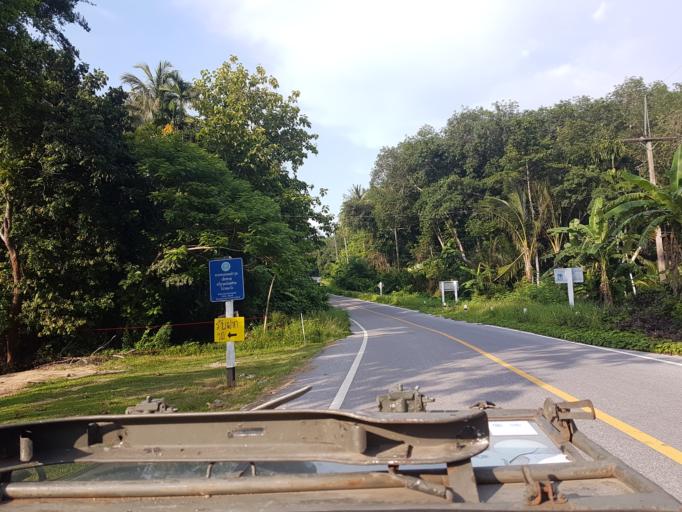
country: TH
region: Pattani
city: Khok Pho
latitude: 6.6600
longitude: 101.0954
